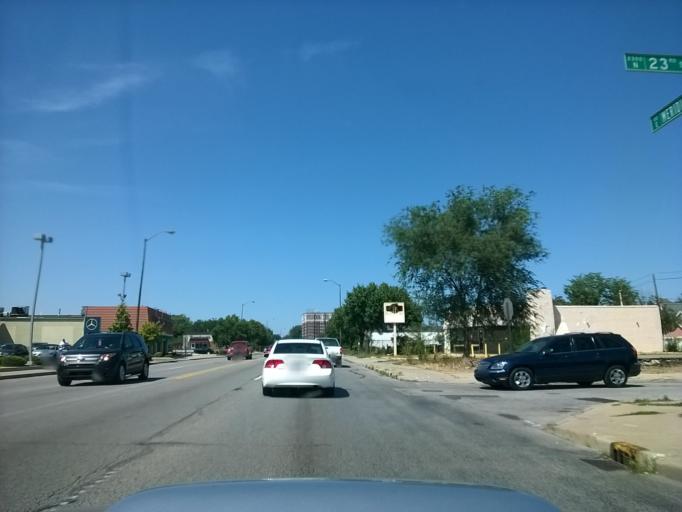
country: US
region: Indiana
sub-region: Marion County
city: Indianapolis
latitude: 39.7991
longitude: -86.1570
